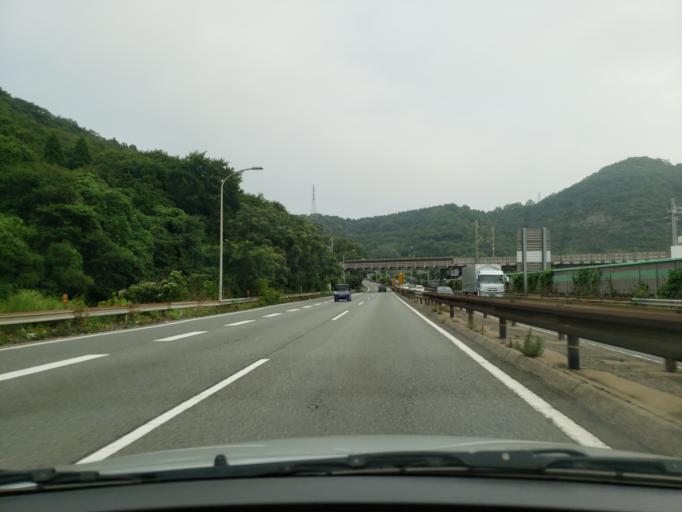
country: JP
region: Hyogo
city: Himeji
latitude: 34.8299
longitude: 134.6327
